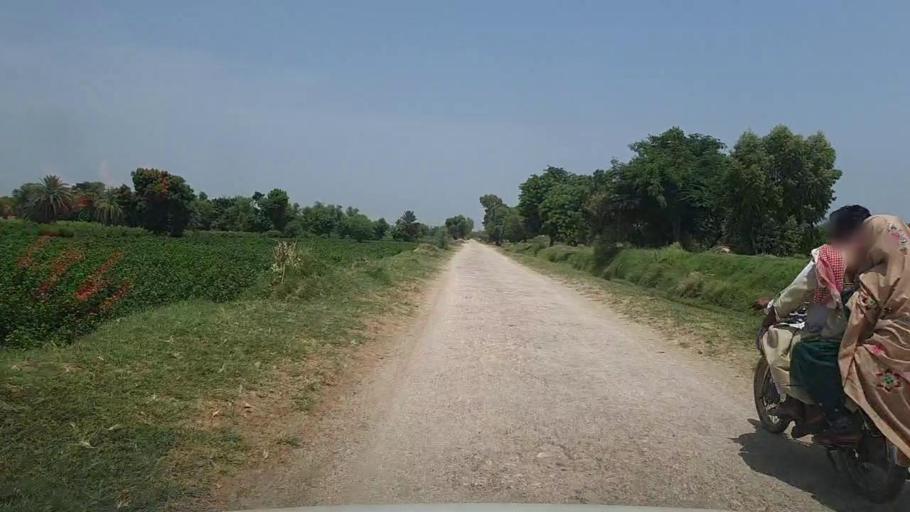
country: PK
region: Sindh
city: Karaundi
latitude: 26.8936
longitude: 68.3325
